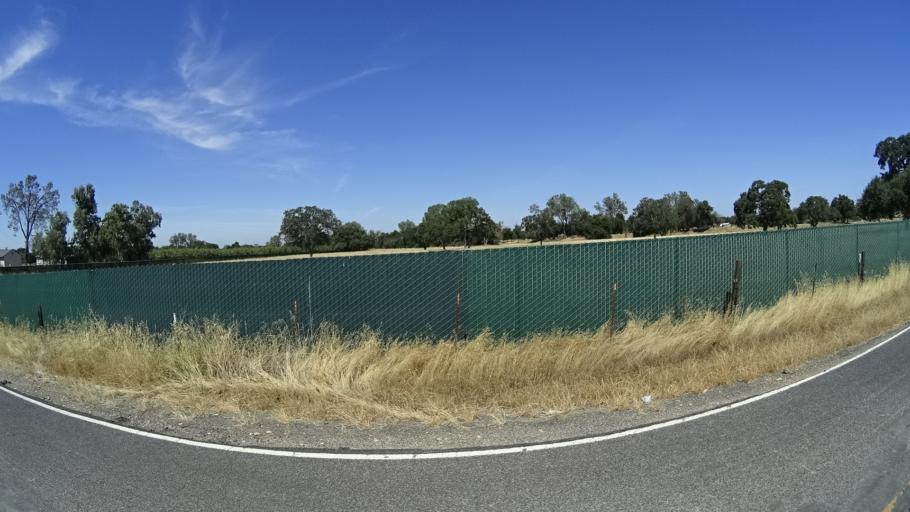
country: US
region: California
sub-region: Calaveras County
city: Rancho Calaveras
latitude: 38.1785
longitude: -120.8906
